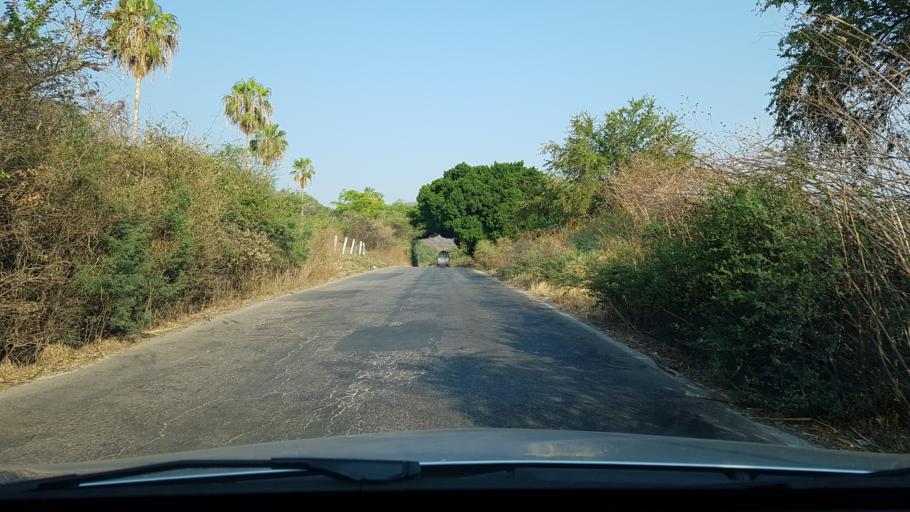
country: MX
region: Morelos
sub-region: Tepalcingo
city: Zacapalco
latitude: 18.6525
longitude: -99.0323
